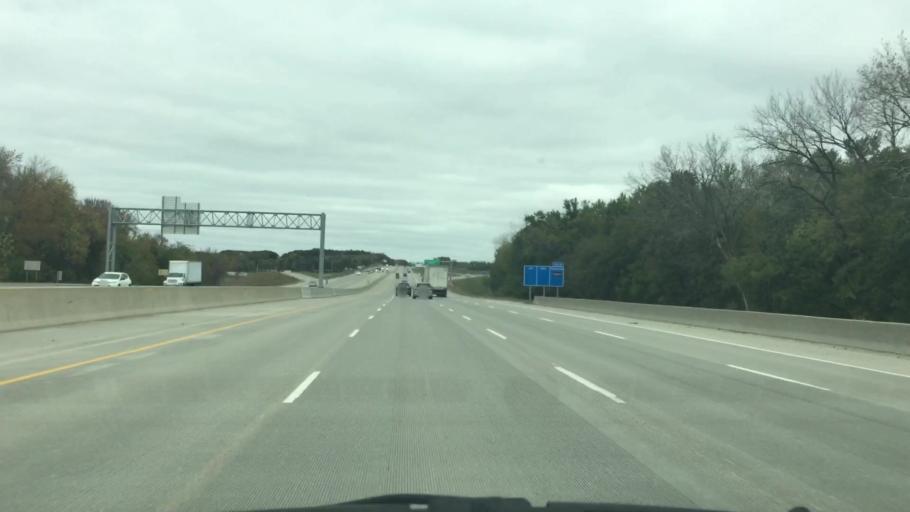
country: US
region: Iowa
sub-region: Polk County
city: West Des Moines
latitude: 41.5333
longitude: -93.7741
